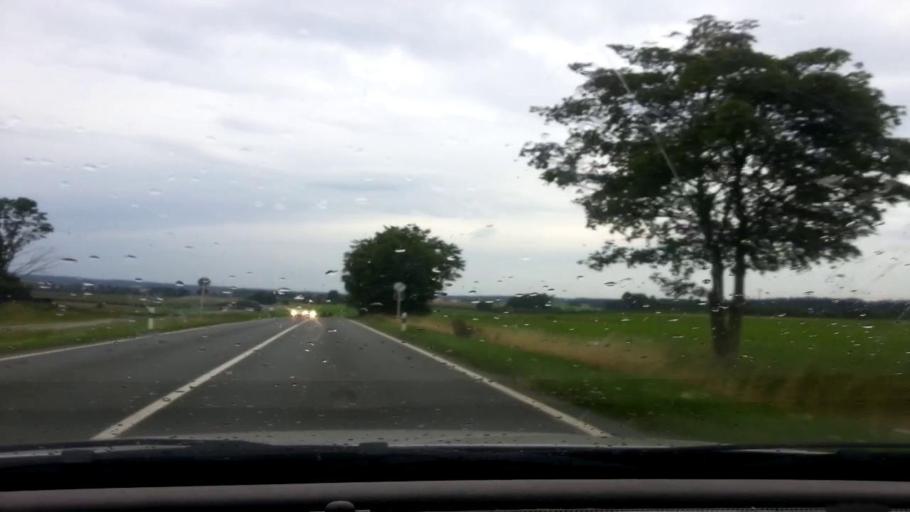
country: DE
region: Bavaria
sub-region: Upper Franconia
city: Speichersdorf
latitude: 49.8771
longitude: 11.8126
